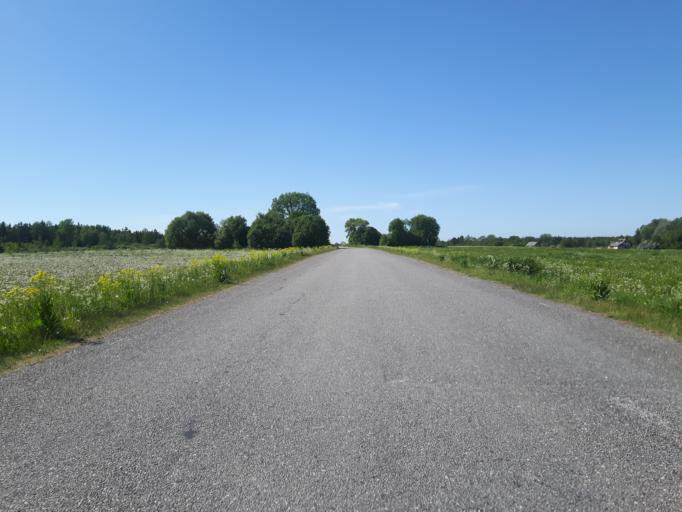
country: EE
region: Laeaene-Virumaa
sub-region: Haljala vald
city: Haljala
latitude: 59.5410
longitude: 26.2257
